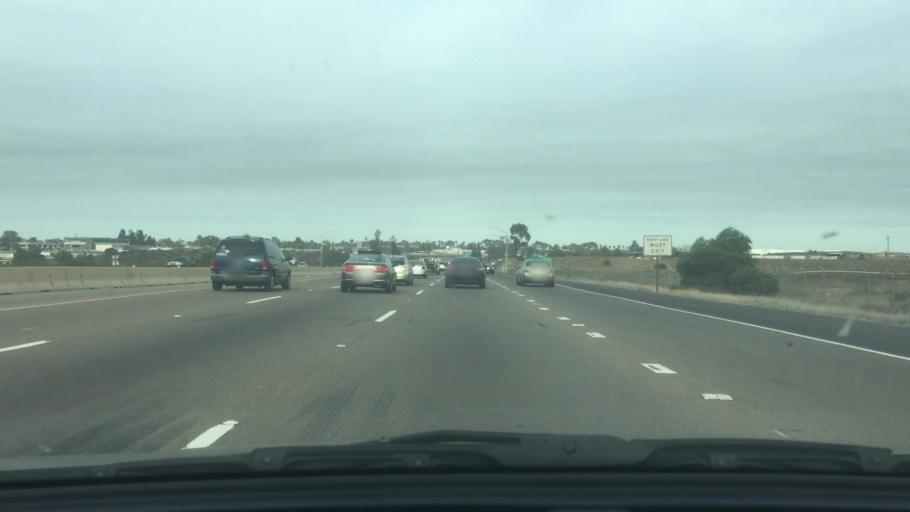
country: US
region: California
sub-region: San Diego County
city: San Diego
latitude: 32.8394
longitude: -117.1446
